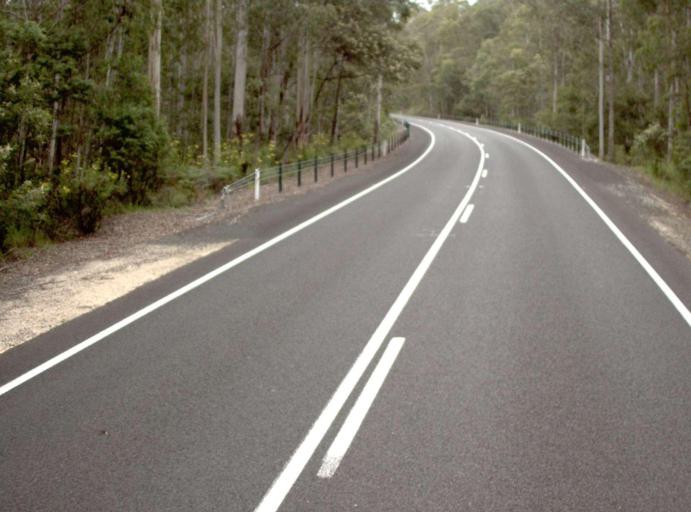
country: AU
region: New South Wales
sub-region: Bombala
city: Bombala
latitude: -37.3062
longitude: 149.2094
